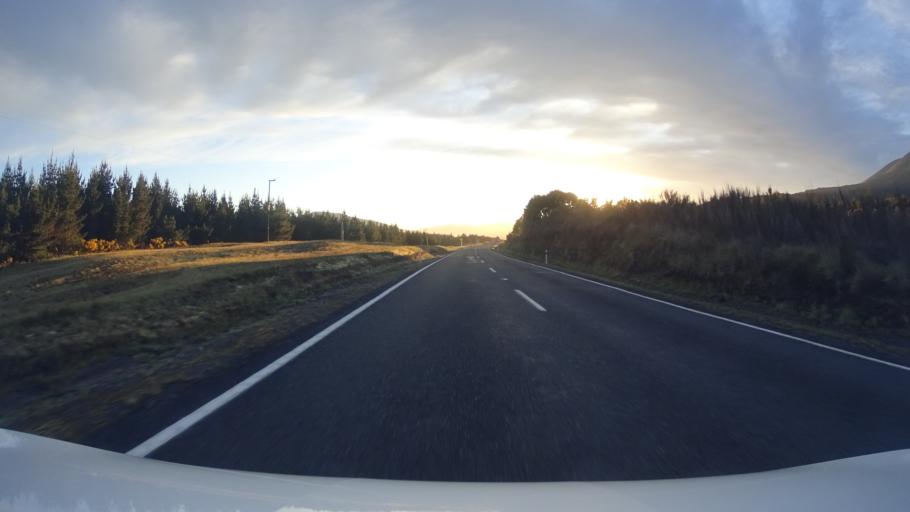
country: NZ
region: Waikato
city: Turangi
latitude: -39.0649
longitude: 175.6622
